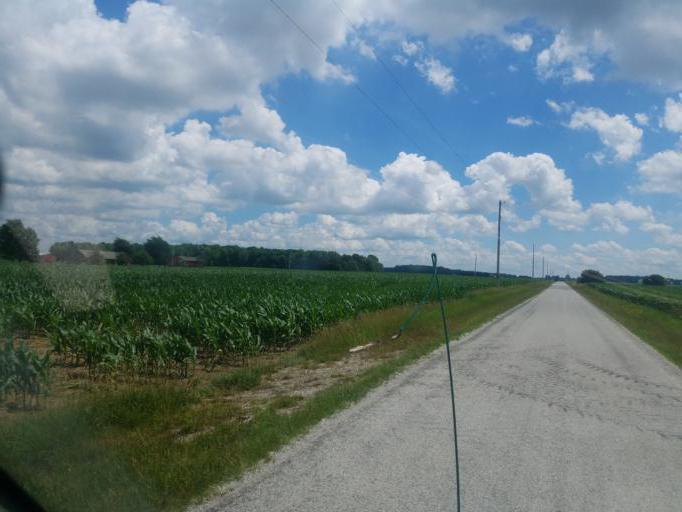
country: US
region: Ohio
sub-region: Huron County
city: Willard
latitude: 40.9867
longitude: -82.8351
